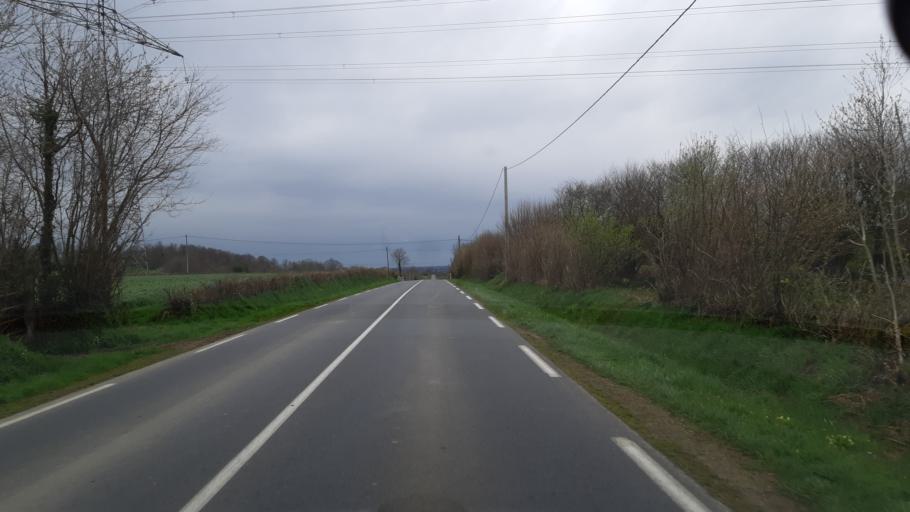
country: FR
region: Lower Normandy
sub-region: Departement de la Manche
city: Hambye
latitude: 48.9539
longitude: -1.2214
